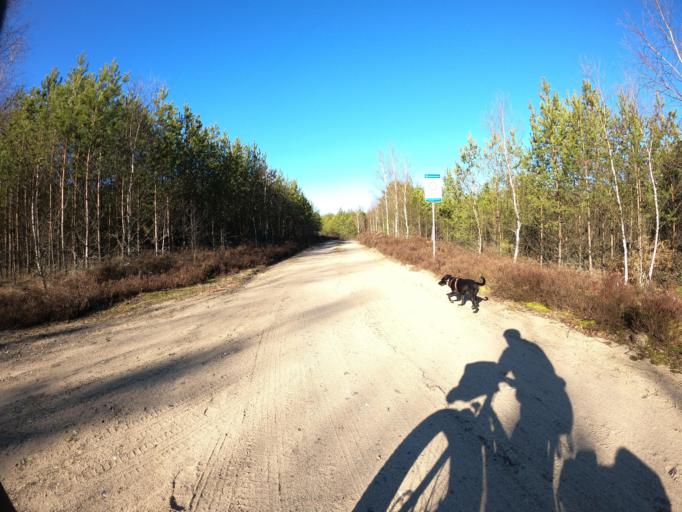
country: PL
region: West Pomeranian Voivodeship
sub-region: Powiat szczecinecki
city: Borne Sulinowo
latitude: 53.5514
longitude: 16.5399
